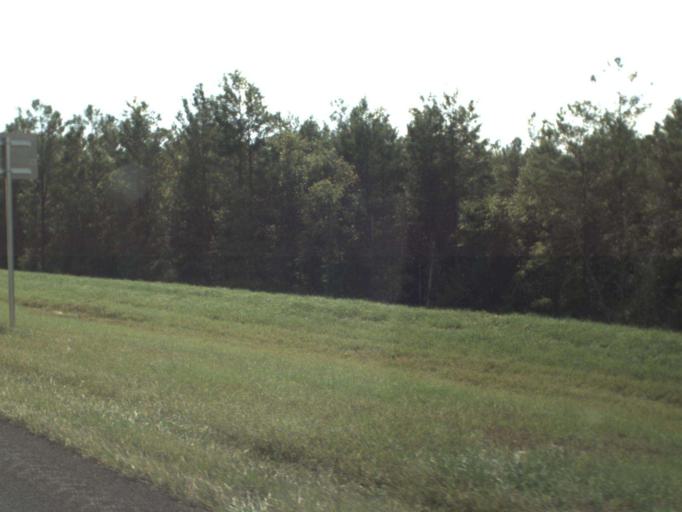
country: US
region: Florida
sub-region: Bay County
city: Laguna Beach
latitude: 30.4991
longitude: -85.8415
